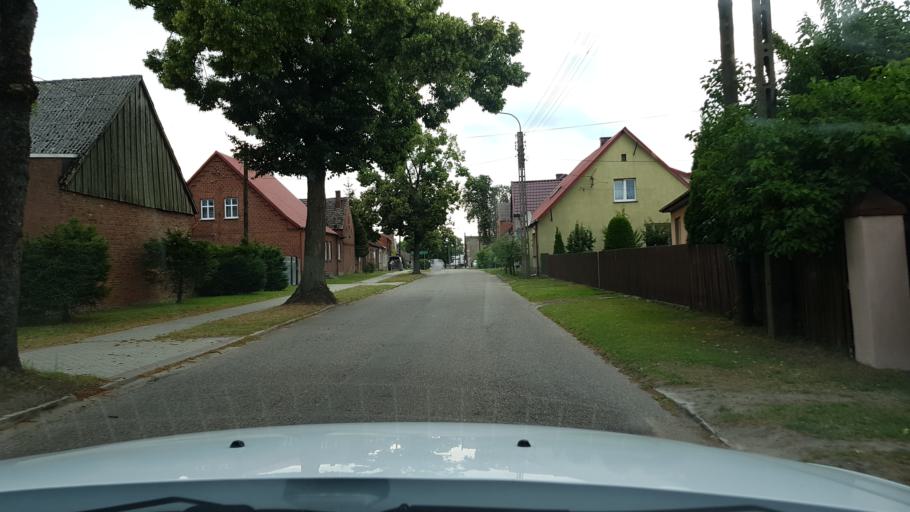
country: PL
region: West Pomeranian Voivodeship
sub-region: Powiat drawski
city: Wierzchowo
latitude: 53.4580
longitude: 16.1061
